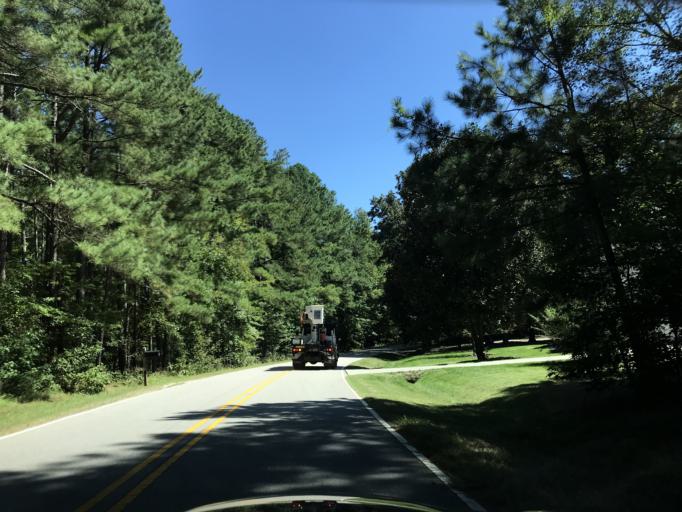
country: US
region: North Carolina
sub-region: Wake County
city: Wake Forest
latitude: 35.9487
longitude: -78.5922
